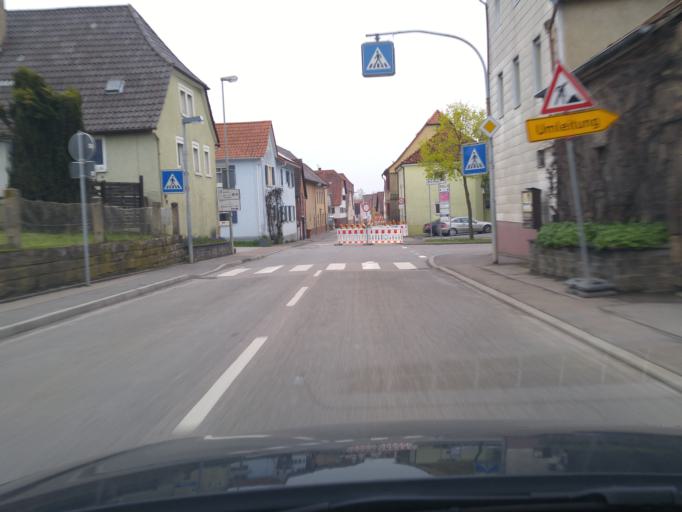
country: DE
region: Baden-Wuerttemberg
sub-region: Regierungsbezirk Stuttgart
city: Siegelsbach
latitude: 49.2714
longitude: 9.0897
